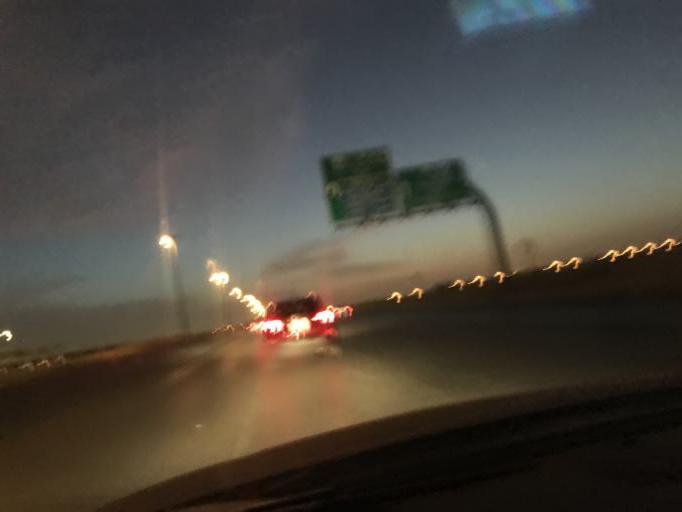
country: SA
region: Ar Riyad
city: Riyadh
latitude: 24.6656
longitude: 46.7808
